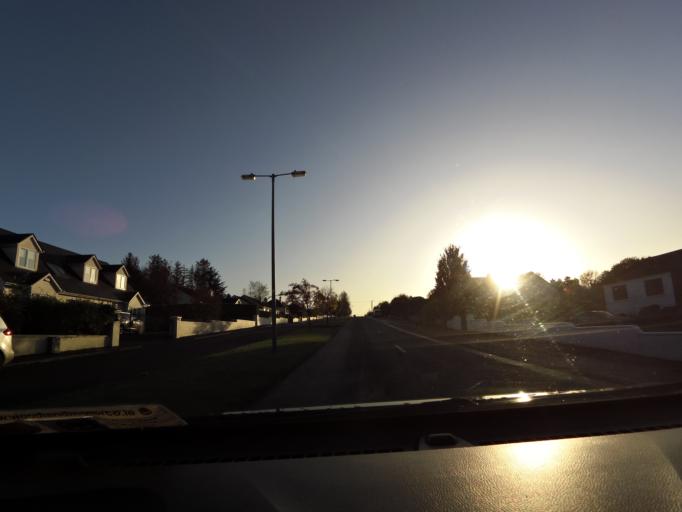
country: IE
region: Connaught
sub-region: Roscommon
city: Castlerea
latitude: 53.7593
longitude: -8.5141
